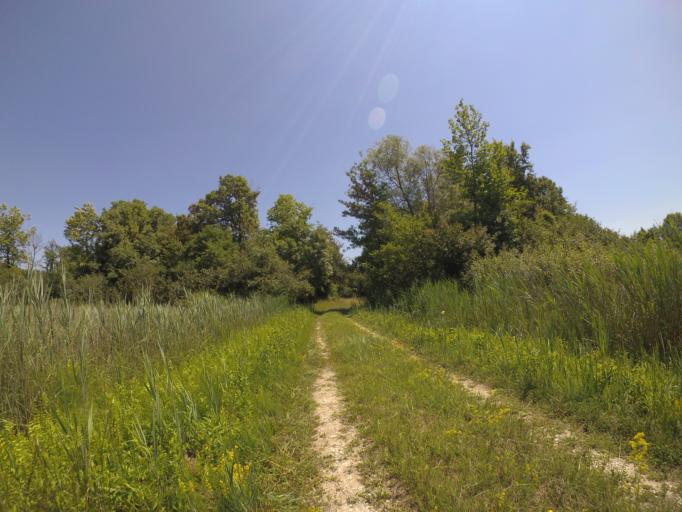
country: IT
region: Friuli Venezia Giulia
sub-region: Provincia di Udine
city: Bertiolo
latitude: 45.9200
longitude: 13.0799
